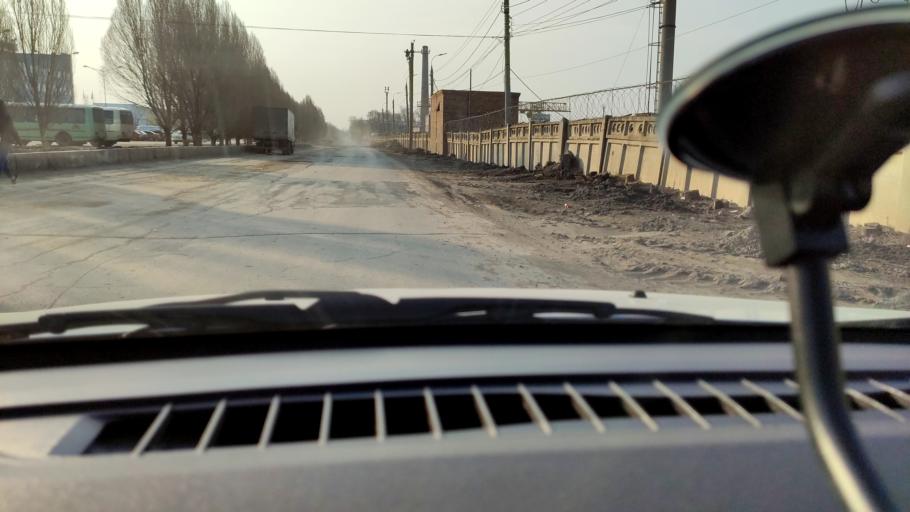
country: RU
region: Samara
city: Samara
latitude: 53.1846
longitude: 50.2608
